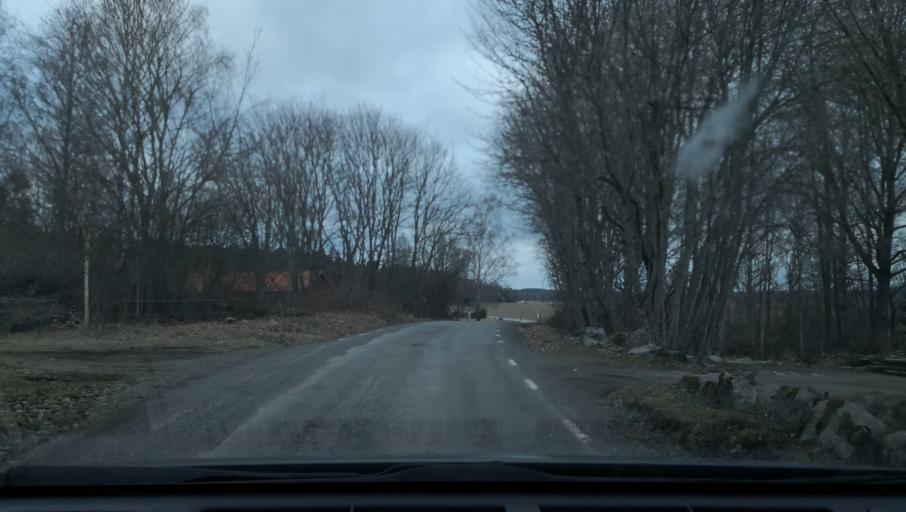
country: SE
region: Vaestmanland
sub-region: Kopings Kommun
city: Kolsva
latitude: 59.5494
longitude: 15.8790
